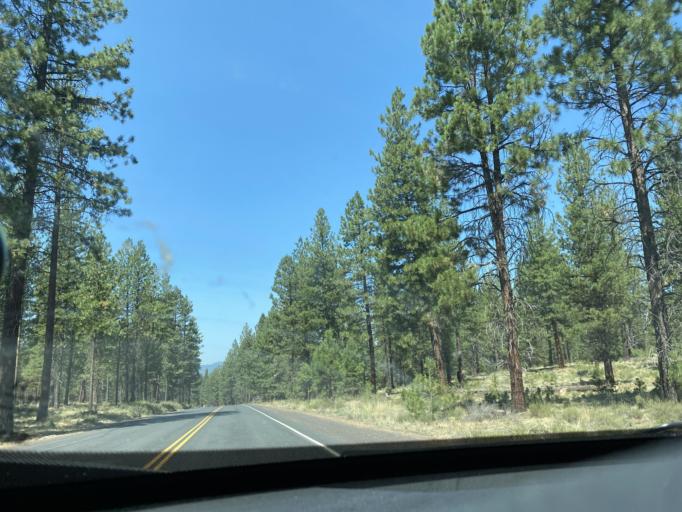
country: US
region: Oregon
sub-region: Deschutes County
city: Sunriver
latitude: 43.8894
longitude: -121.3999
